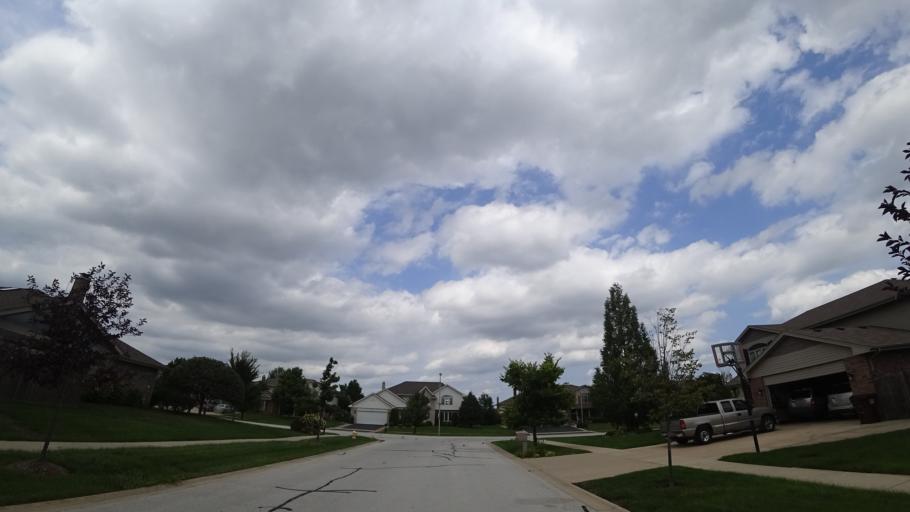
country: US
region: Illinois
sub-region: Cook County
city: Orland Hills
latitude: 41.5592
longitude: -87.8270
